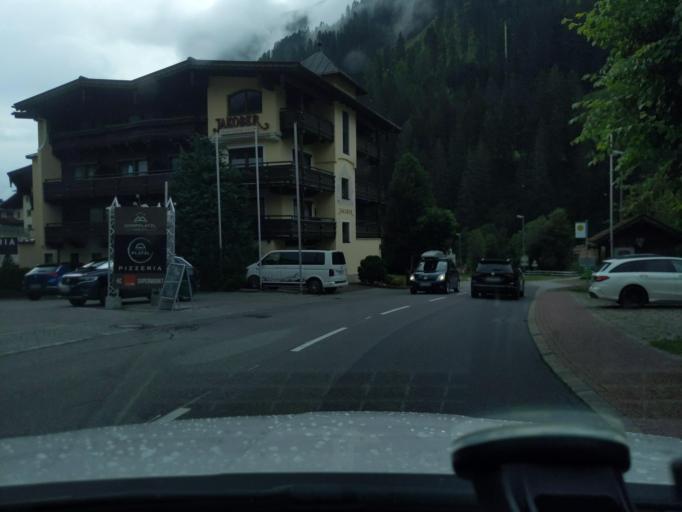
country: AT
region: Tyrol
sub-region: Politischer Bezirk Schwaz
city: Schwendau
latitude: 47.1625
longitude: 11.7447
